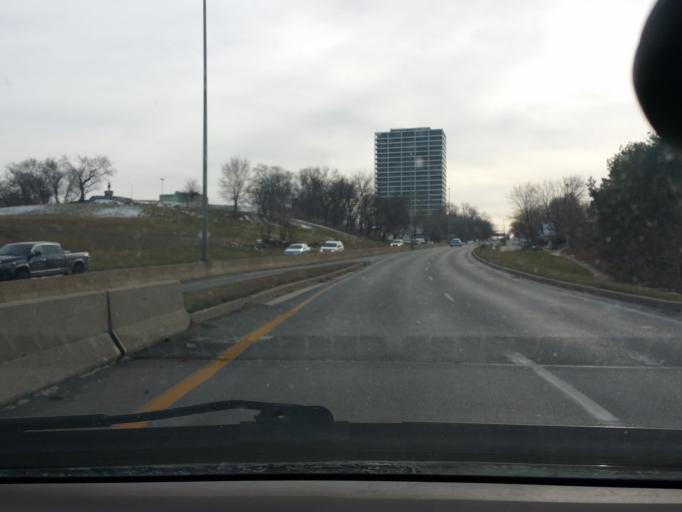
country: US
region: Missouri
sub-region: Jackson County
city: Kansas City
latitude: 39.0778
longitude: -94.5942
